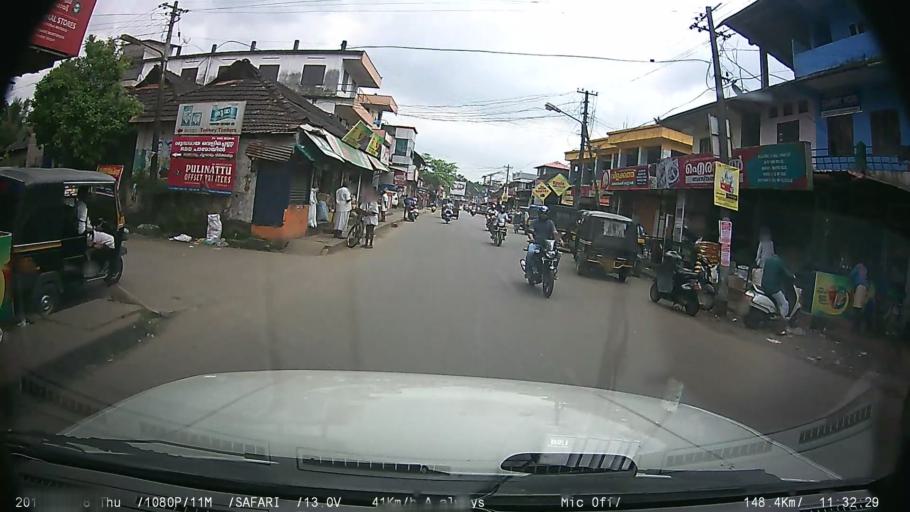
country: IN
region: Kerala
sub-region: Ernakulam
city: Muvattupula
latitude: 9.9902
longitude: 76.5826
